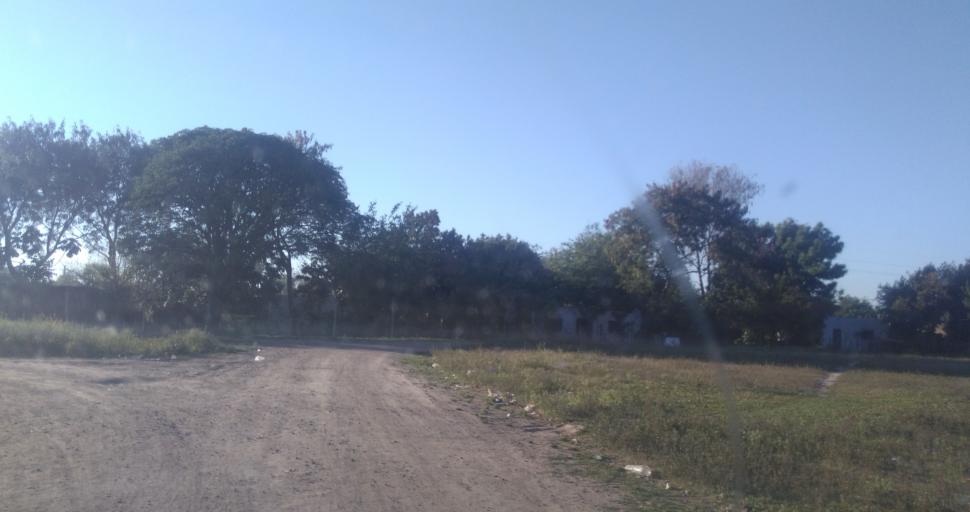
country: AR
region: Chaco
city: Fontana
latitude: -27.4249
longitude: -59.0178
